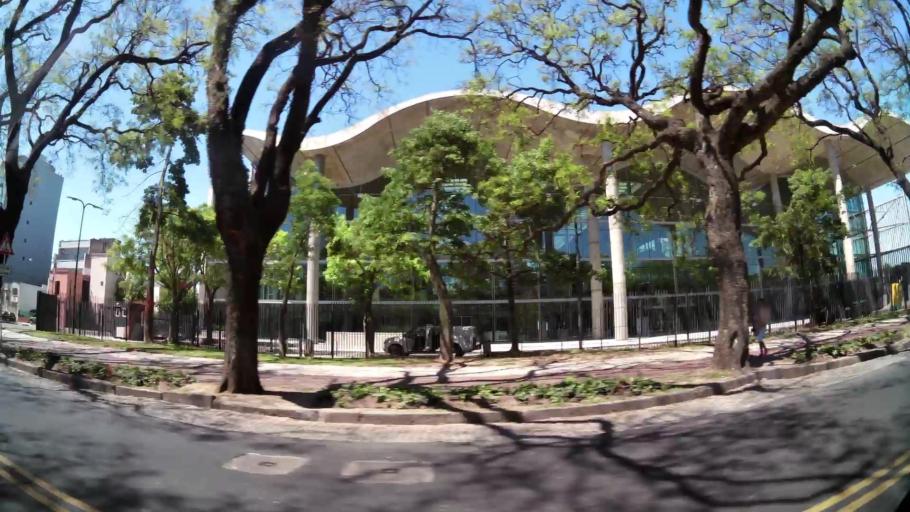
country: AR
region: Buenos Aires F.D.
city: Buenos Aires
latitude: -34.6401
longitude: -58.4070
